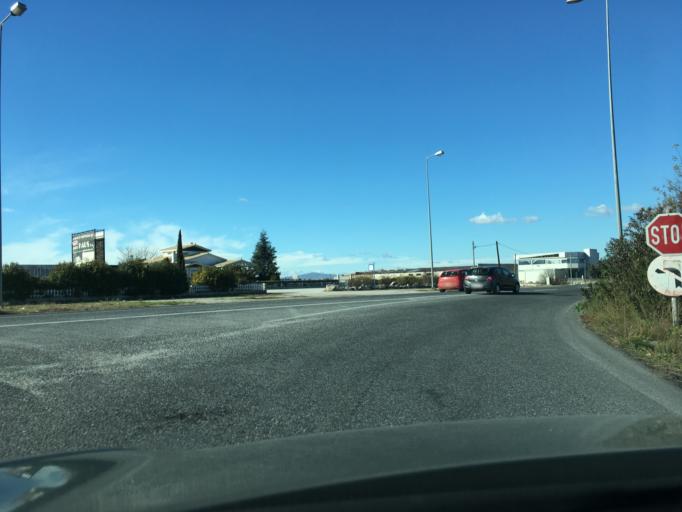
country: GR
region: Thessaly
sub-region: Nomos Larisis
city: Nikaia
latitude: 39.5982
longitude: 22.4478
